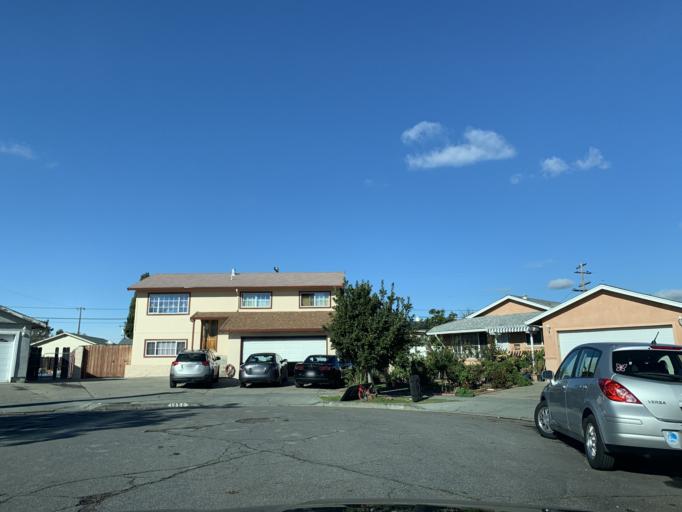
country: US
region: California
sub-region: Santa Clara County
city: Alum Rock
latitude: 37.3432
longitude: -121.8348
